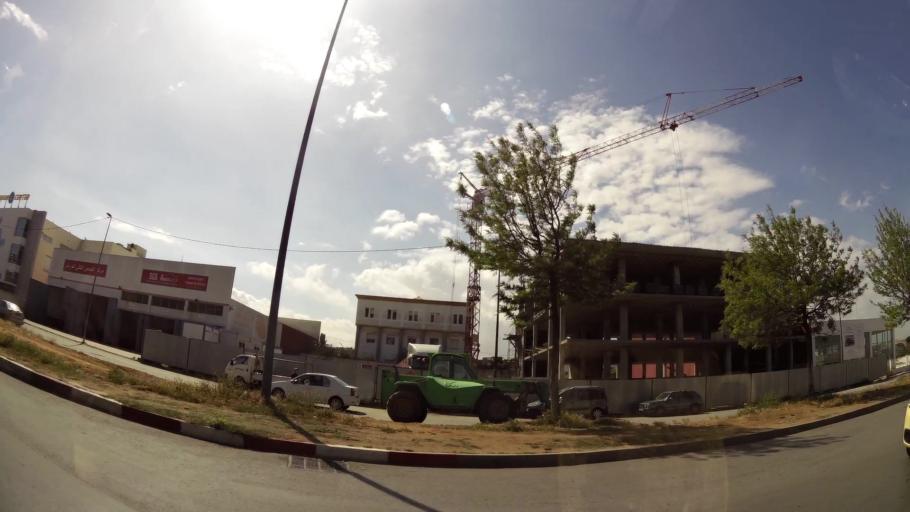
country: MA
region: Rabat-Sale-Zemmour-Zaer
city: Sale
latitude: 34.0671
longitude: -6.7934
